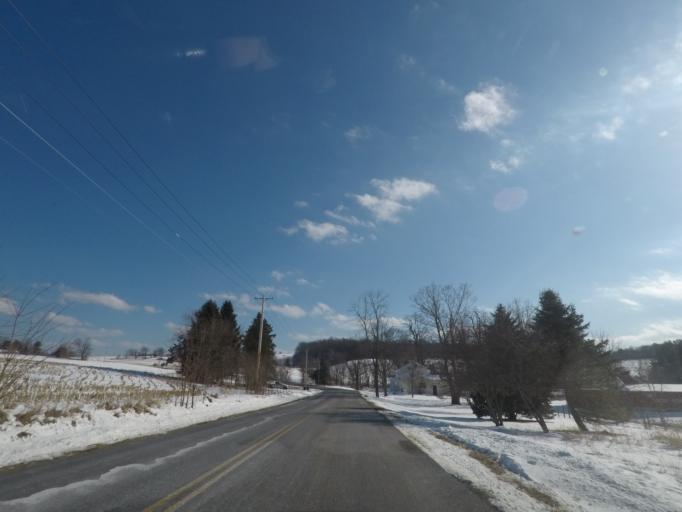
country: US
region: New York
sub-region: Rensselaer County
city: Hoosick Falls
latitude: 42.8730
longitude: -73.4979
